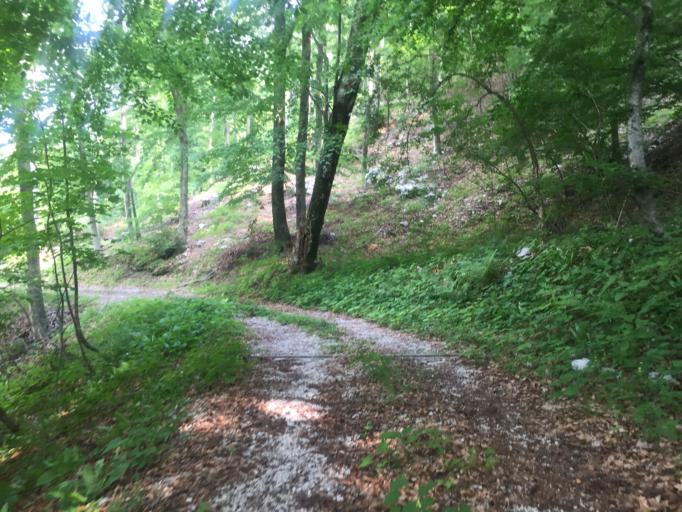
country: IT
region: Friuli Venezia Giulia
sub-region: Provincia di Udine
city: Cavazzo Carnico
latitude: 46.3497
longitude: 13.0232
